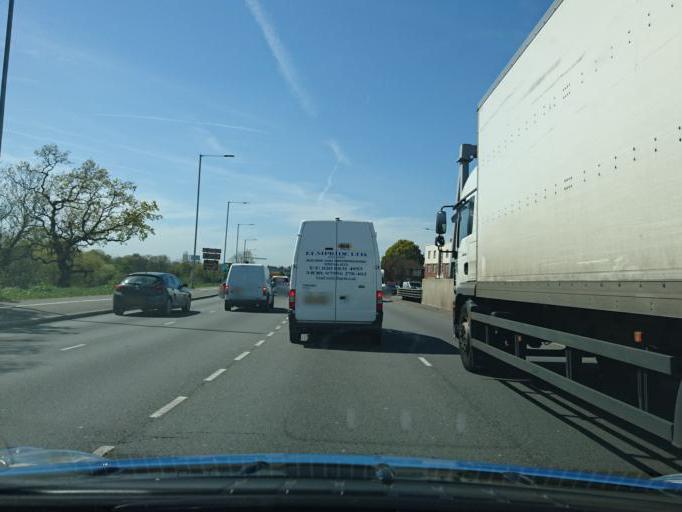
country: GB
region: England
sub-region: Greater London
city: Hendon
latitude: 51.5896
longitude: -0.2014
